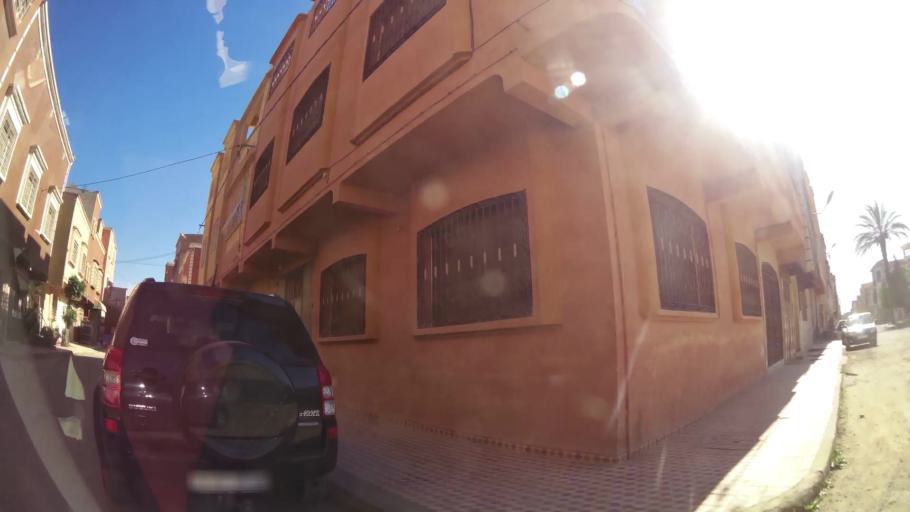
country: MA
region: Oriental
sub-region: Berkane-Taourirt
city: Berkane
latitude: 34.9395
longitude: -2.3355
